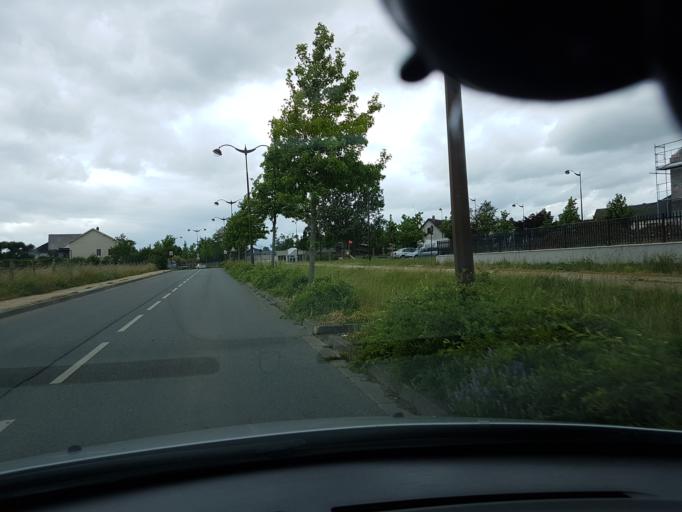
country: FR
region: Centre
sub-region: Departement du Cher
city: Bourges
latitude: 47.1090
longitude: 2.4190
